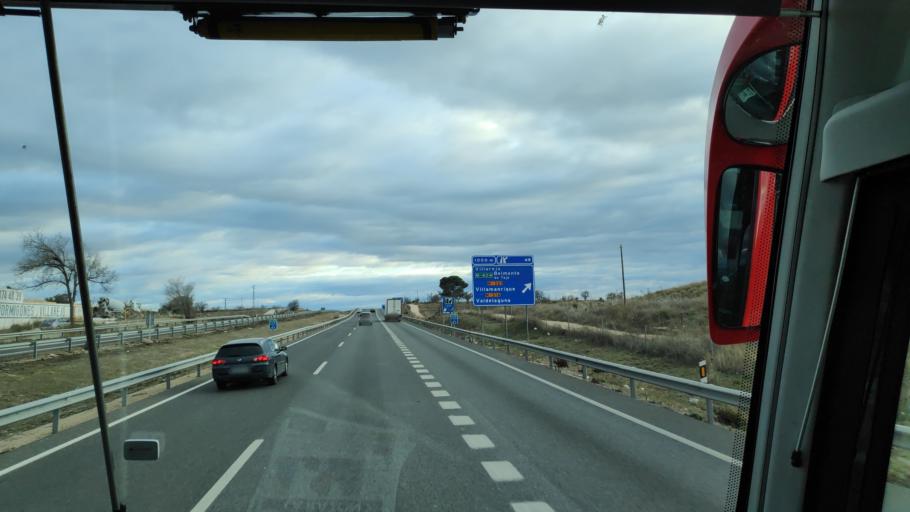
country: ES
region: Madrid
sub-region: Provincia de Madrid
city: Villarejo de Salvanes
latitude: 40.1849
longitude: -3.2979
